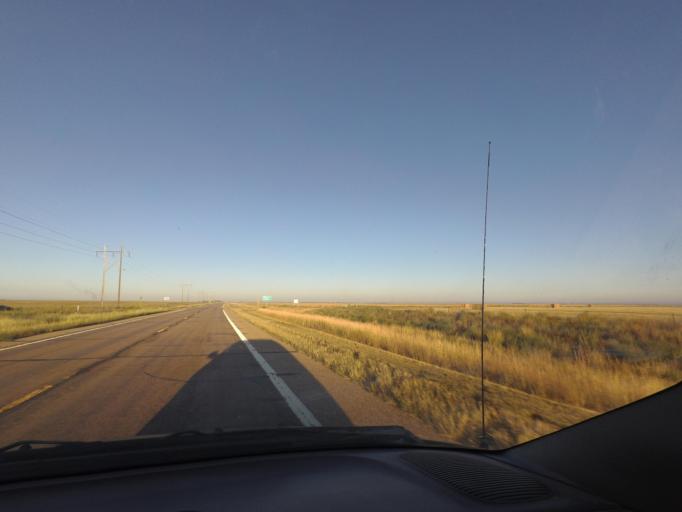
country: US
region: Colorado
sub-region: Yuma County
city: Yuma
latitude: 39.6549
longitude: -102.8010
